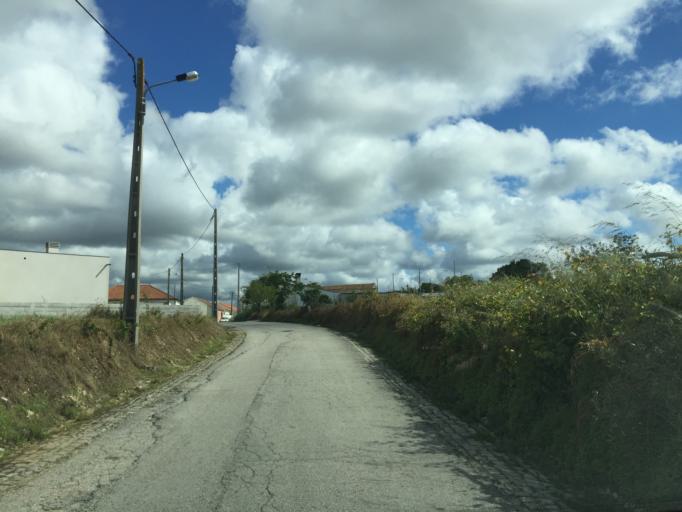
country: PT
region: Leiria
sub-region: Pombal
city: Lourical
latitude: 39.9843
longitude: -8.8060
